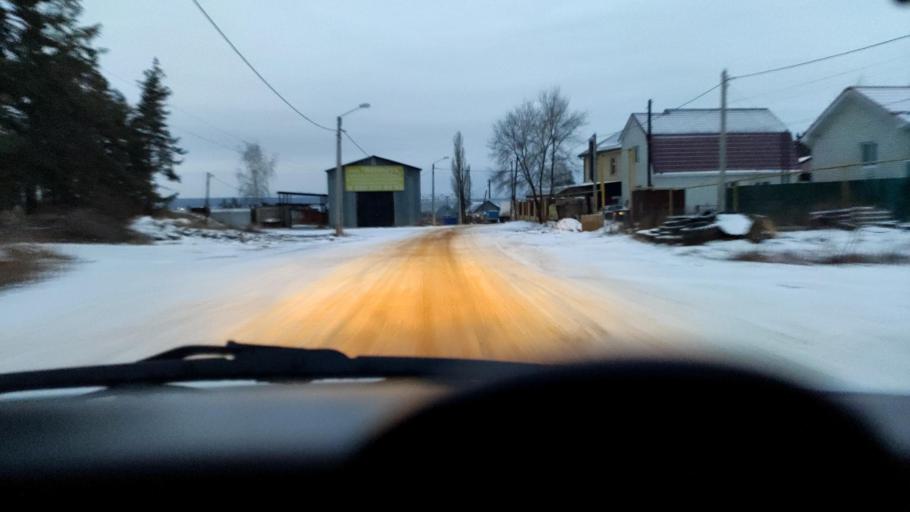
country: RU
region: Voronezj
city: Pridonskoy
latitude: 51.7004
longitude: 39.1053
